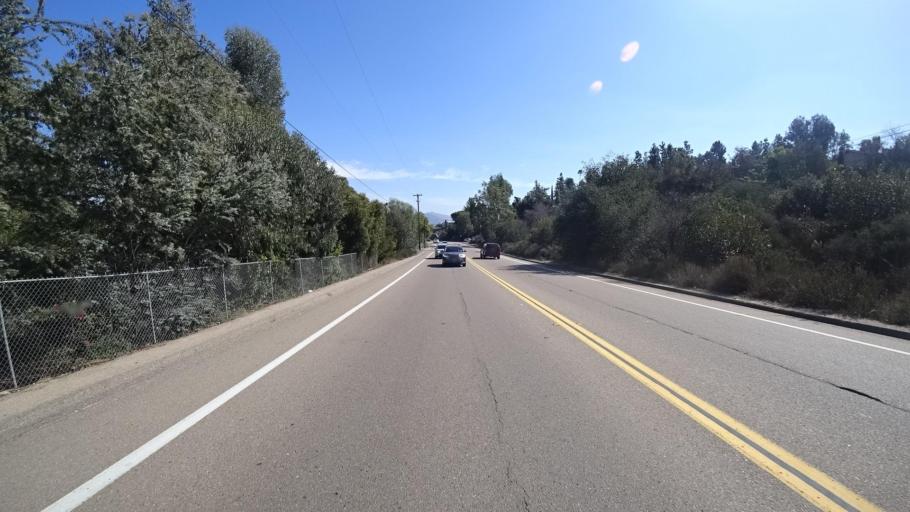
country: US
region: California
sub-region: San Diego County
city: Rancho San Diego
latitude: 32.7702
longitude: -116.9341
